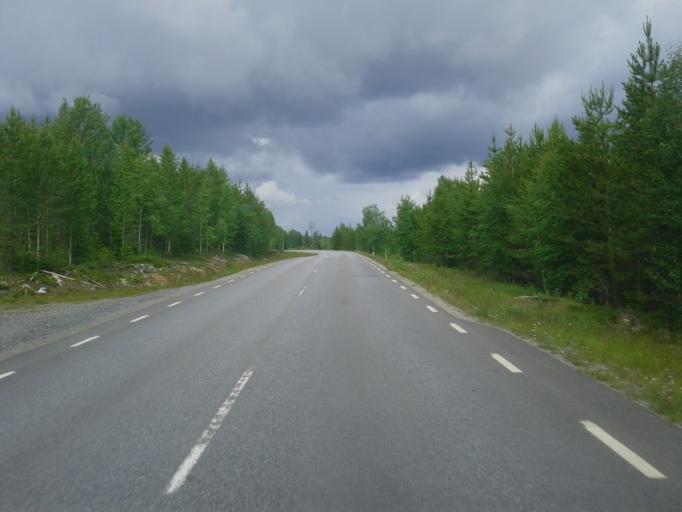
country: SE
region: Vaesterbotten
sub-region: Norsjo Kommun
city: Norsjoe
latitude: 65.0125
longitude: 19.1381
